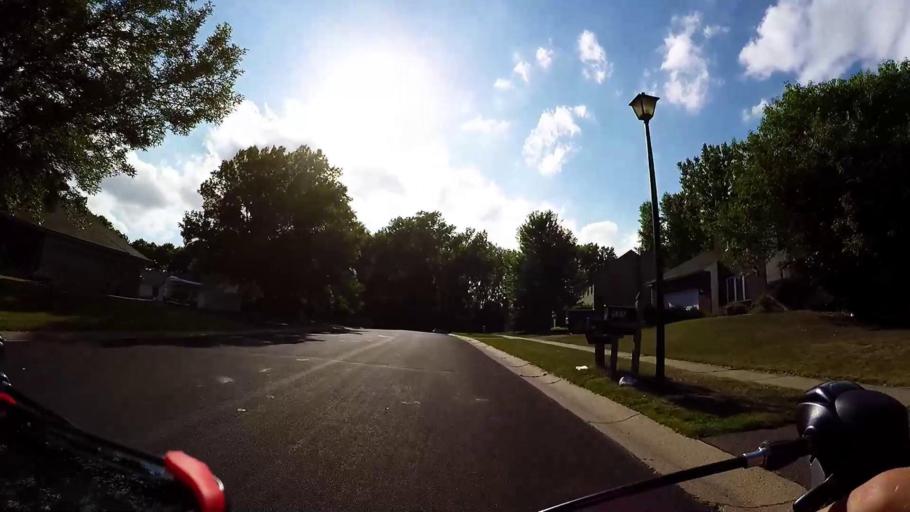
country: US
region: Minnesota
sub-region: Hennepin County
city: Eden Prairie
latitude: 44.8833
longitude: -93.4446
